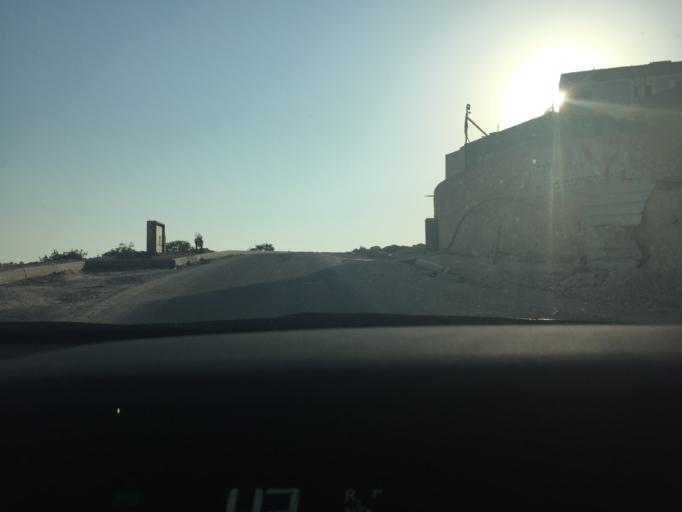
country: PS
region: West Bank
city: Rafat
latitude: 32.0662
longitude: 35.0490
